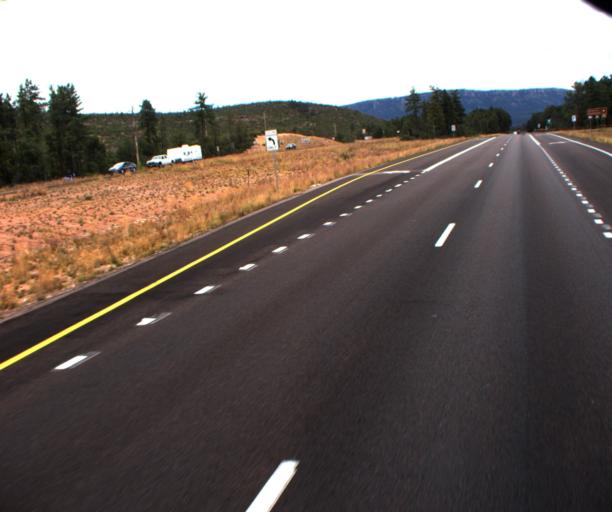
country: US
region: Arizona
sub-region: Gila County
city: Star Valley
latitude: 34.2971
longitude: -111.1207
